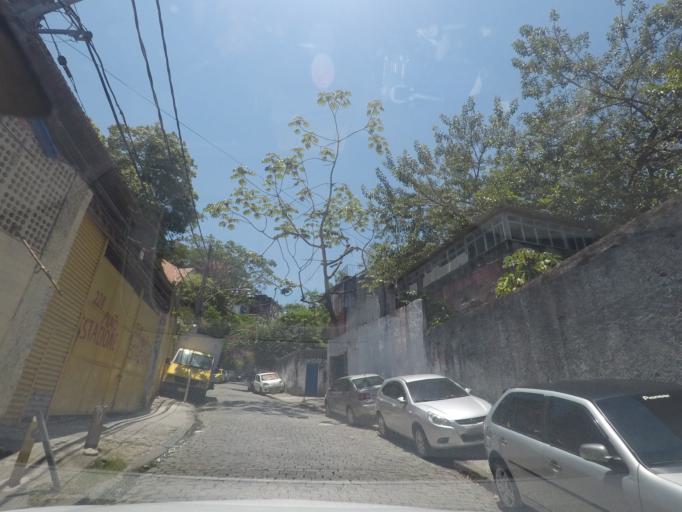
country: BR
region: Rio de Janeiro
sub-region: Rio De Janeiro
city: Rio de Janeiro
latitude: -22.9831
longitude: -43.1956
